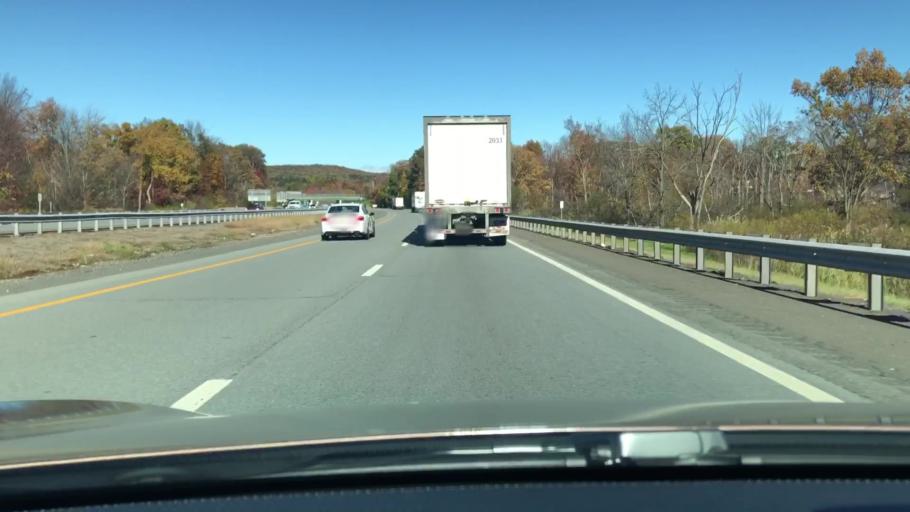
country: US
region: New York
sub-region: Orange County
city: Central Valley
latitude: 41.3212
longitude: -74.1131
